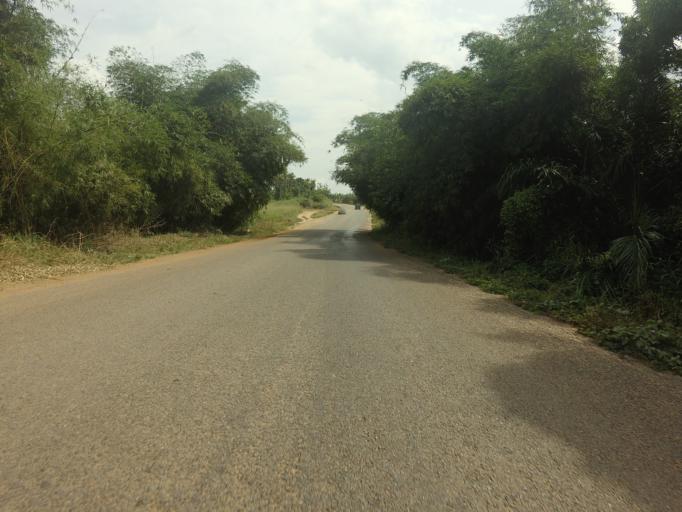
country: GH
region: Eastern
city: Koforidua
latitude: 5.9716
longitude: -0.2263
